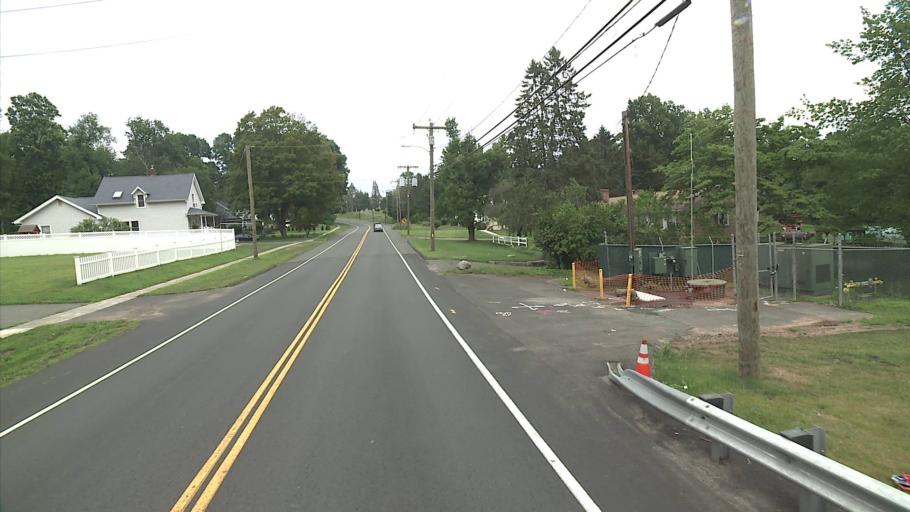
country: US
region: Connecticut
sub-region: Hartford County
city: Wethersfield
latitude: 41.6571
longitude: -72.6400
